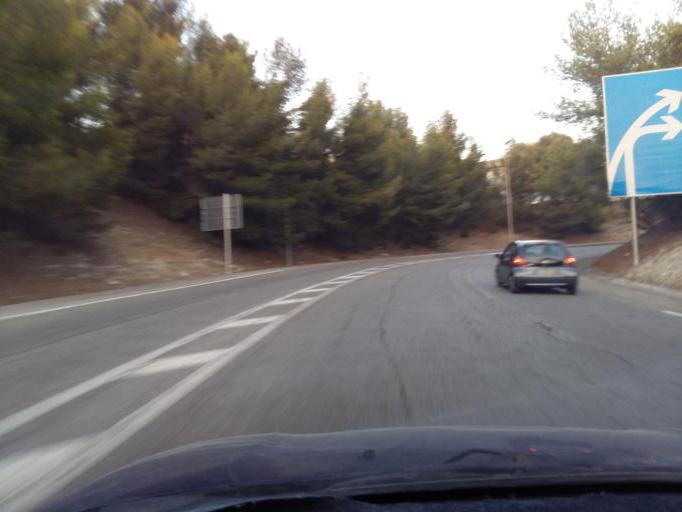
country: FR
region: Provence-Alpes-Cote d'Azur
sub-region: Departement des Bouches-du-Rhone
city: Martigues
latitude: 43.4110
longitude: 5.0379
